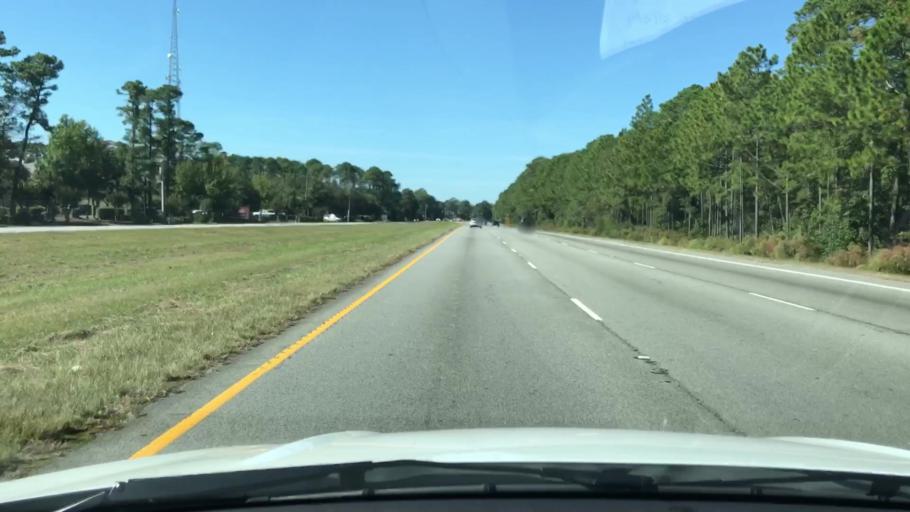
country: US
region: South Carolina
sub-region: Beaufort County
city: Bluffton
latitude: 32.2496
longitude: -80.8371
